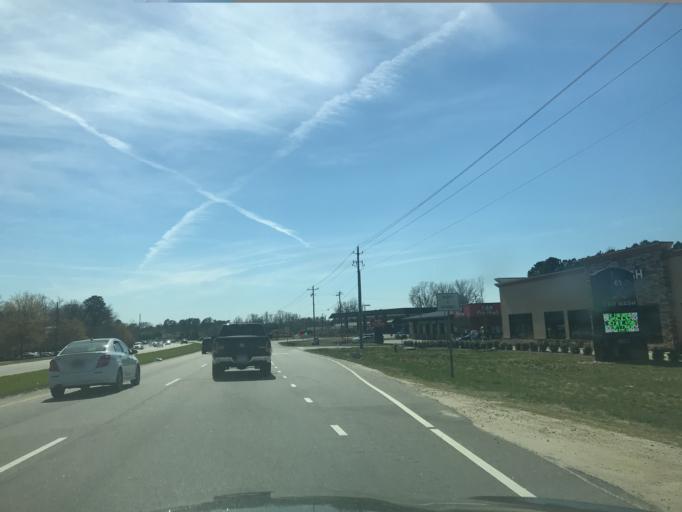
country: US
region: North Carolina
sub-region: Wake County
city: Garner
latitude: 35.6649
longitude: -78.7002
